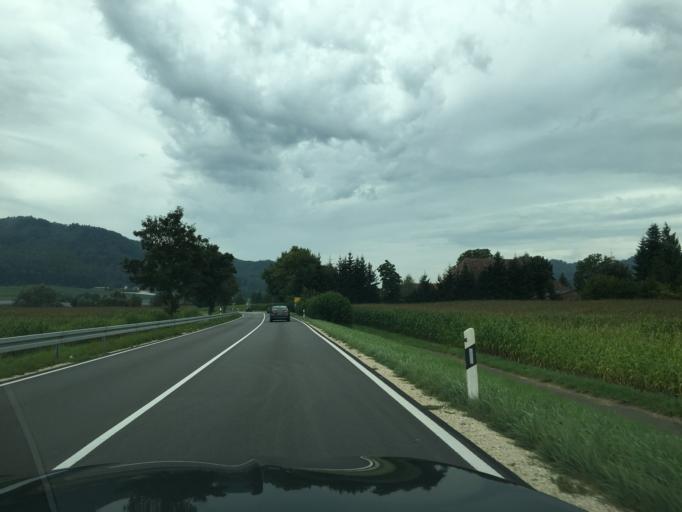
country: DE
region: Baden-Wuerttemberg
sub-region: Freiburg Region
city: Stockach
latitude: 47.8113
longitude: 8.9916
